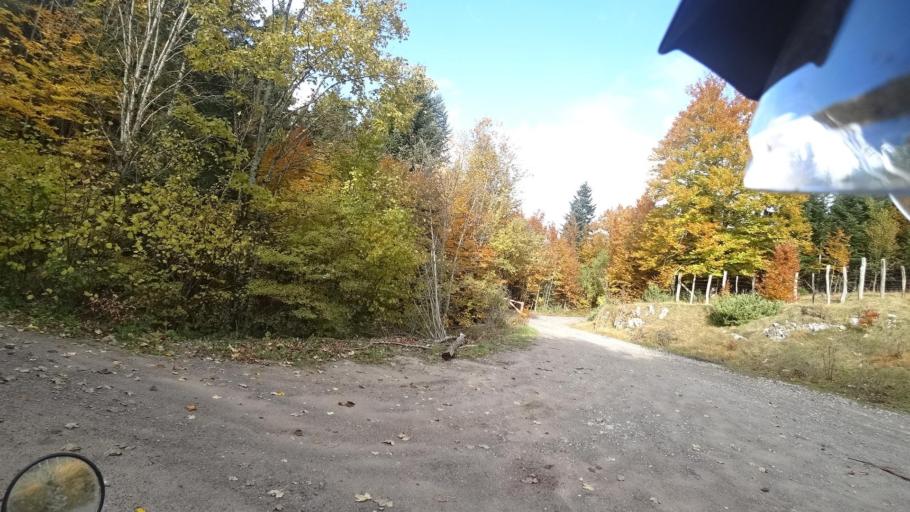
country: HR
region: Karlovacka
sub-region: Grad Ogulin
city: Ogulin
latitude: 45.2044
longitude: 15.1109
